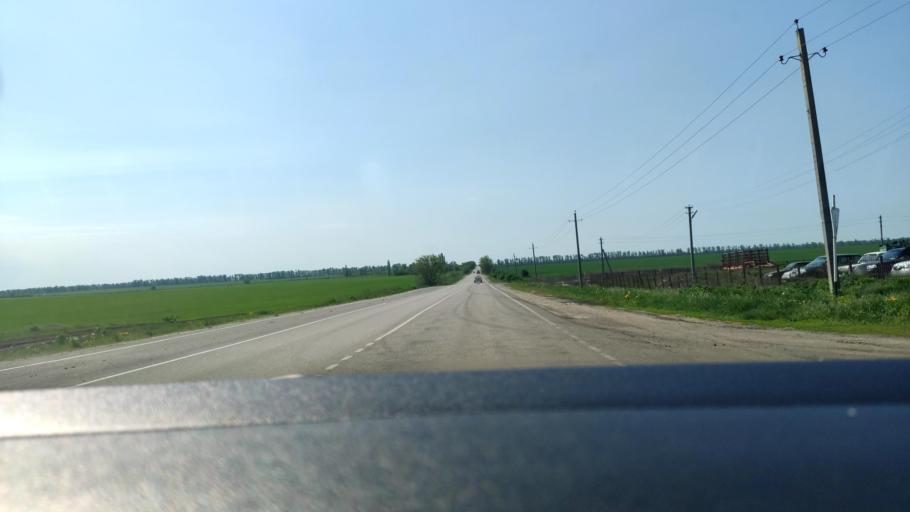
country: RU
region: Voronezj
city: Novaya Usman'
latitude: 51.5807
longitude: 39.3750
